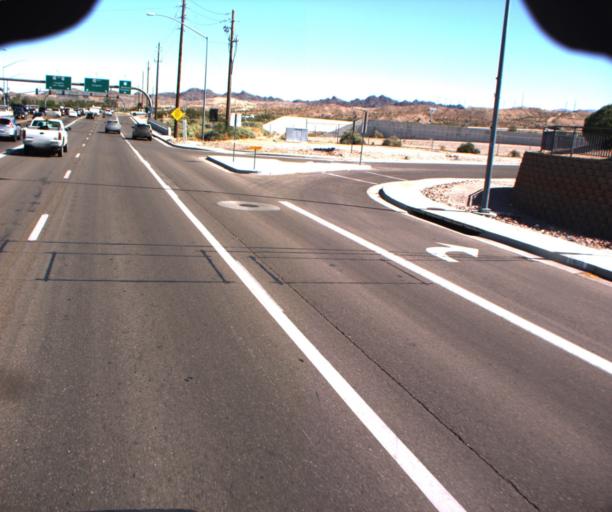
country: US
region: Nevada
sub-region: Clark County
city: Laughlin
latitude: 35.1703
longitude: -114.5659
